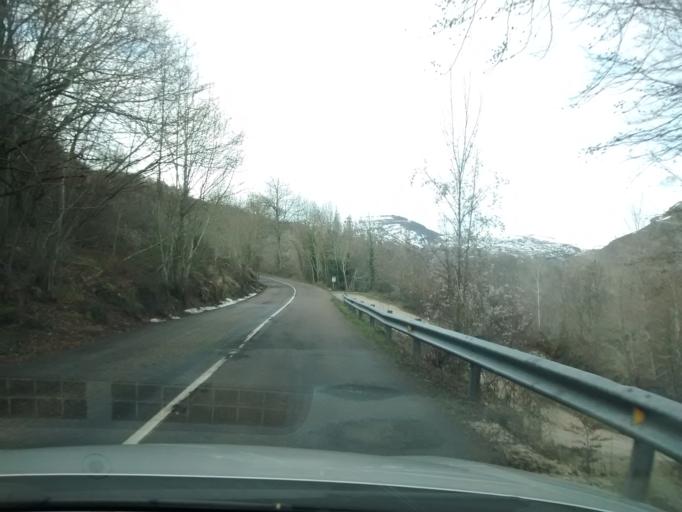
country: ES
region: Castille and Leon
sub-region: Provincia de Burgos
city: Espinosa de los Monteros
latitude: 43.1214
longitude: -3.6022
